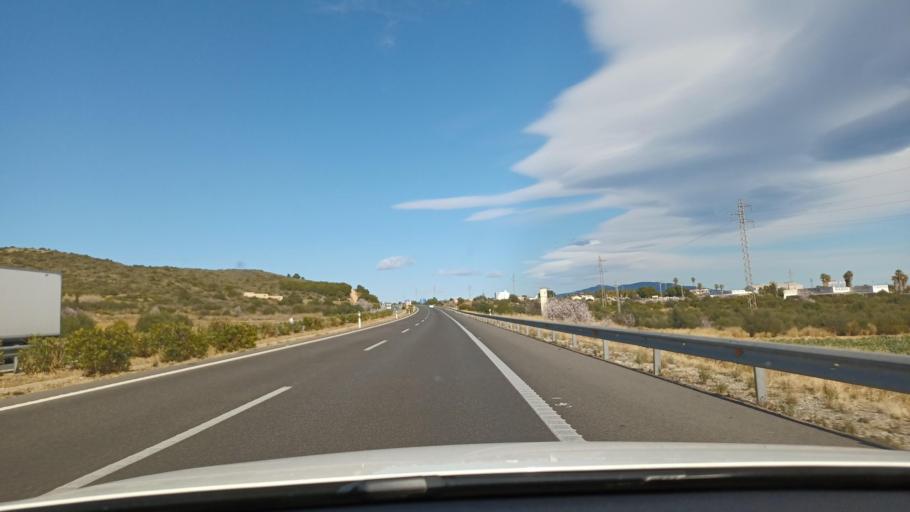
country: ES
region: Valencia
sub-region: Provincia de Castello
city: Torreblanca
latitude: 40.1859
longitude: 0.1694
